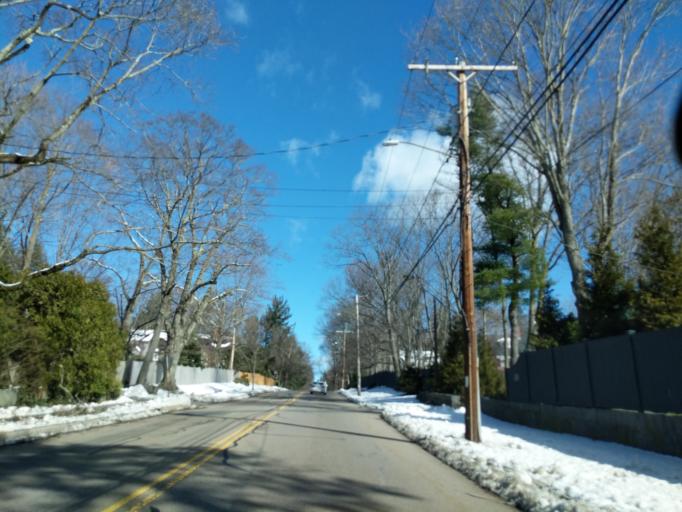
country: US
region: Massachusetts
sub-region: Norfolk County
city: Milton
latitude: 42.2606
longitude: -71.0686
